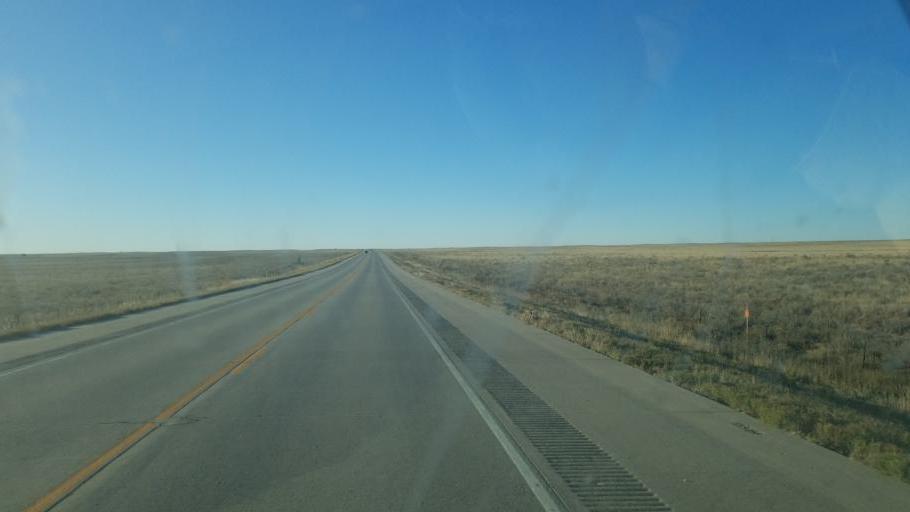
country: US
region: Colorado
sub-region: Kiowa County
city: Eads
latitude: 38.5761
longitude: -102.7862
